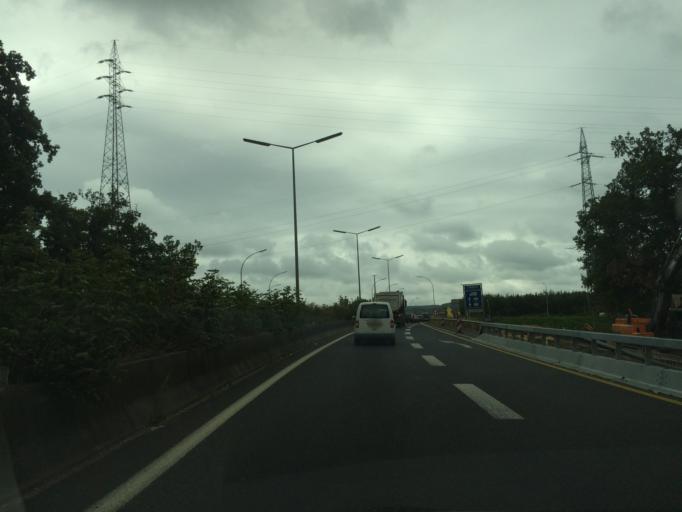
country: LU
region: Luxembourg
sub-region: Canton d'Esch-sur-Alzette
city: Esch-sur-Alzette
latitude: 49.5145
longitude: 5.9752
